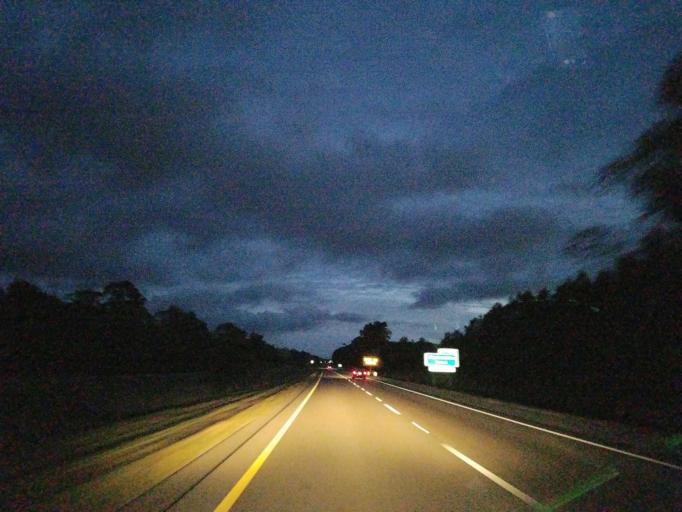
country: US
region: Mississippi
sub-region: Jones County
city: Sharon
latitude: 31.8030
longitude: -89.0541
